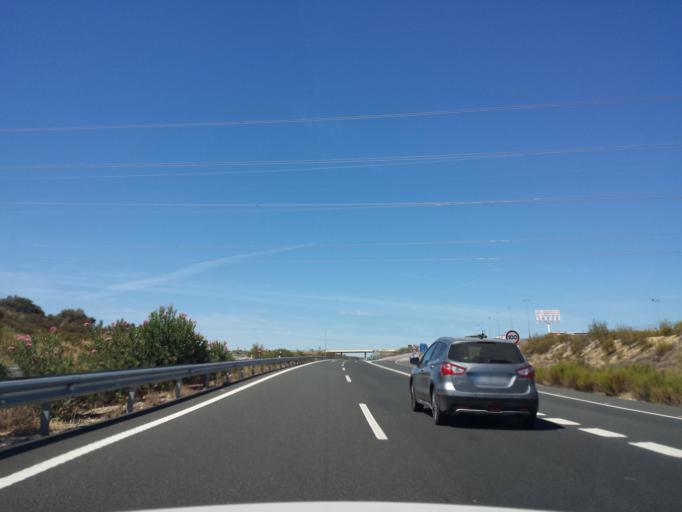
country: ES
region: Extremadura
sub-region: Provincia de Caceres
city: Almaraz
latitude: 39.7910
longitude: -5.6933
